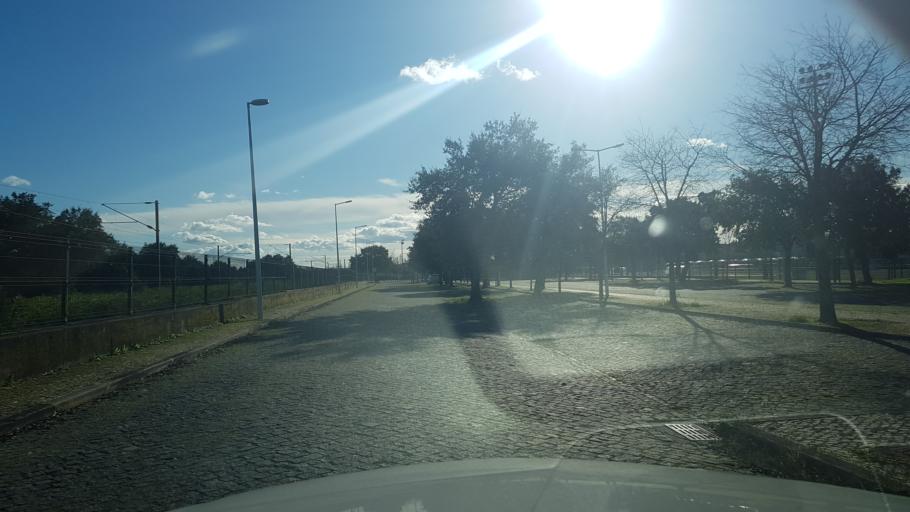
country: PT
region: Santarem
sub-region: Entroncamento
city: Entroncamento
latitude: 39.4765
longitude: -8.4654
